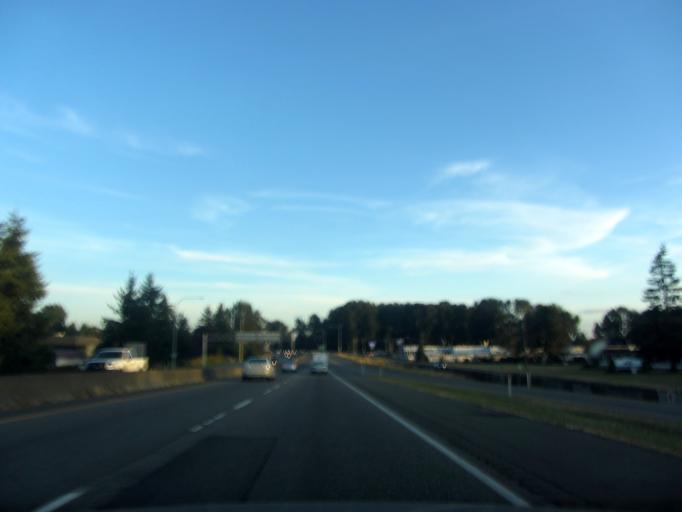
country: US
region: Washington
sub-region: Skagit County
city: Mount Vernon
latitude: 48.4339
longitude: -122.3413
